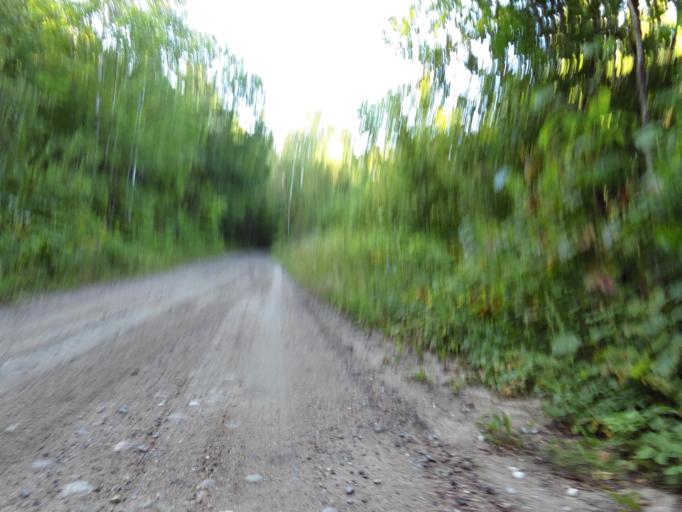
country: CA
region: Quebec
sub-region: Outaouais
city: Maniwaki
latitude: 46.3175
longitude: -76.0069
